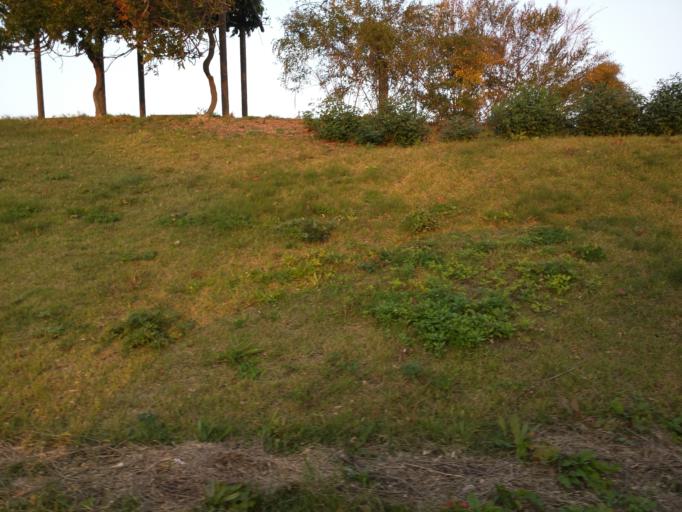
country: JP
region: Fukushima
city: Kitakata
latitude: 37.4779
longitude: 139.8944
